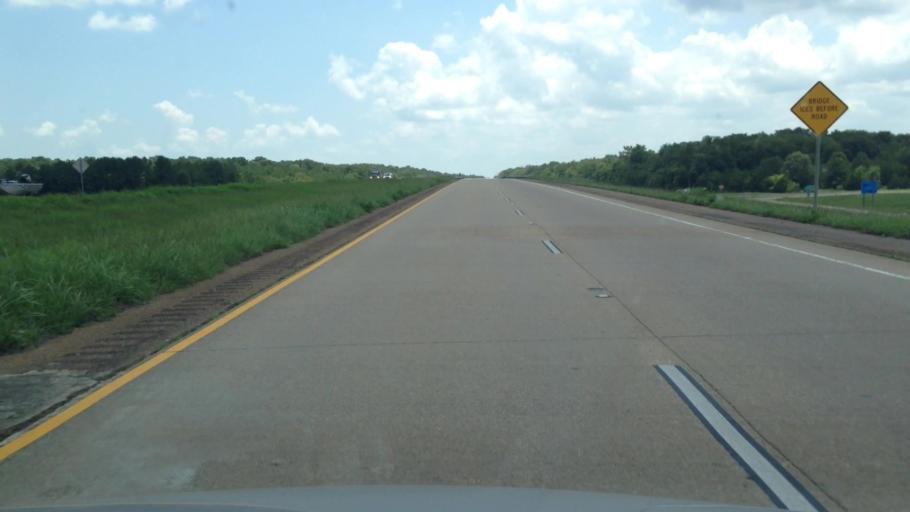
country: US
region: Louisiana
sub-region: Rapides Parish
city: Woodworth
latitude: 31.1669
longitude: -92.4612
